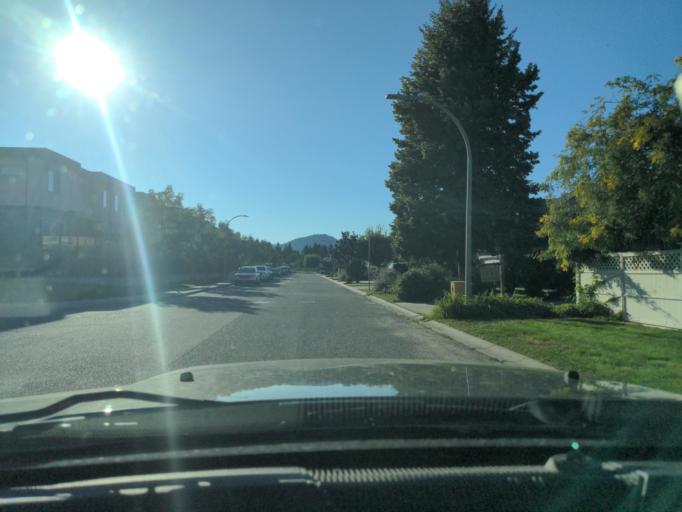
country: CA
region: British Columbia
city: Kelowna
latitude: 49.8542
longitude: -119.4767
